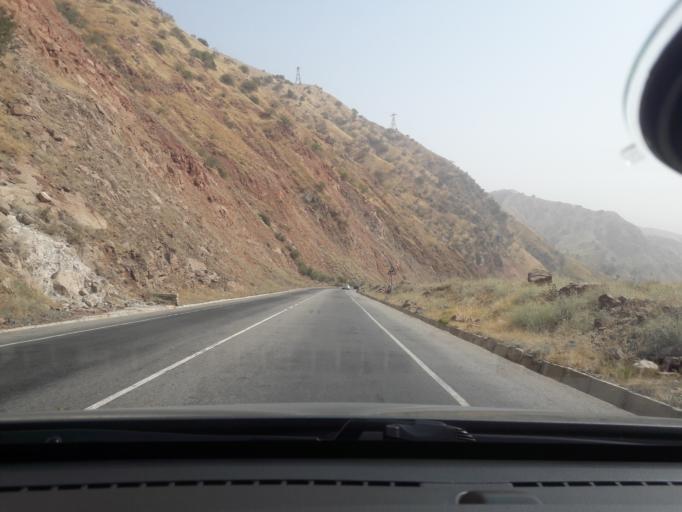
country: TJ
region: Khatlon
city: Norak
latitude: 38.4308
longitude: 69.2178
